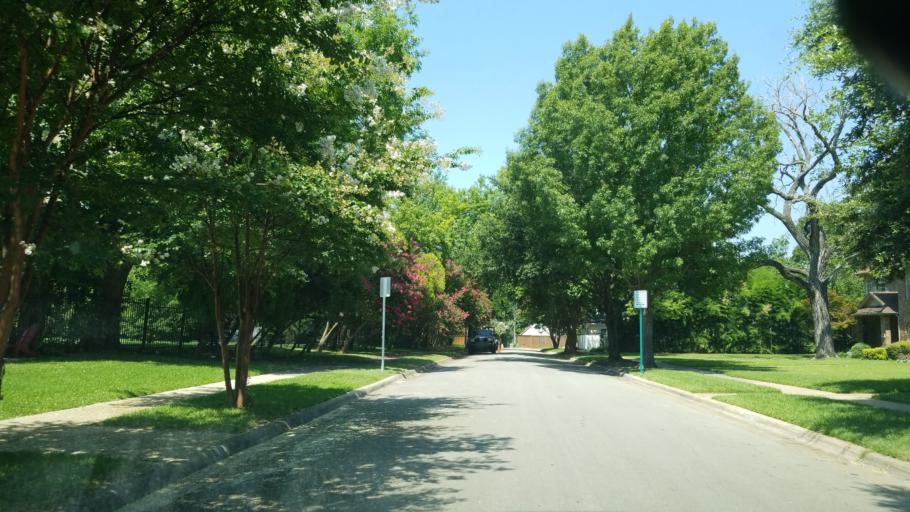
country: US
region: Texas
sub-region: Dallas County
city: Highland Park
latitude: 32.8488
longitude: -96.7816
